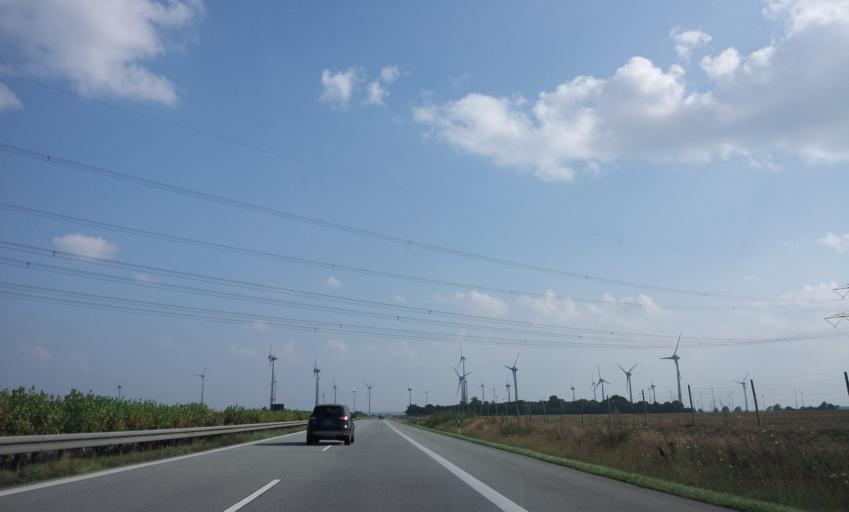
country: DE
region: Mecklenburg-Vorpommern
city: Kessin
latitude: 53.7480
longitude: 13.3339
